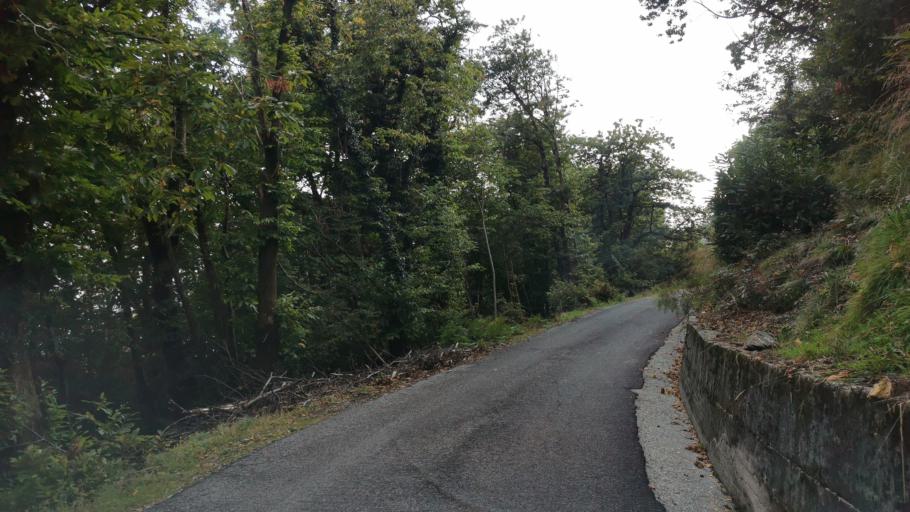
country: IT
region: Lombardy
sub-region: Provincia di Como
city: San Siro
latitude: 46.0735
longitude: 9.2556
